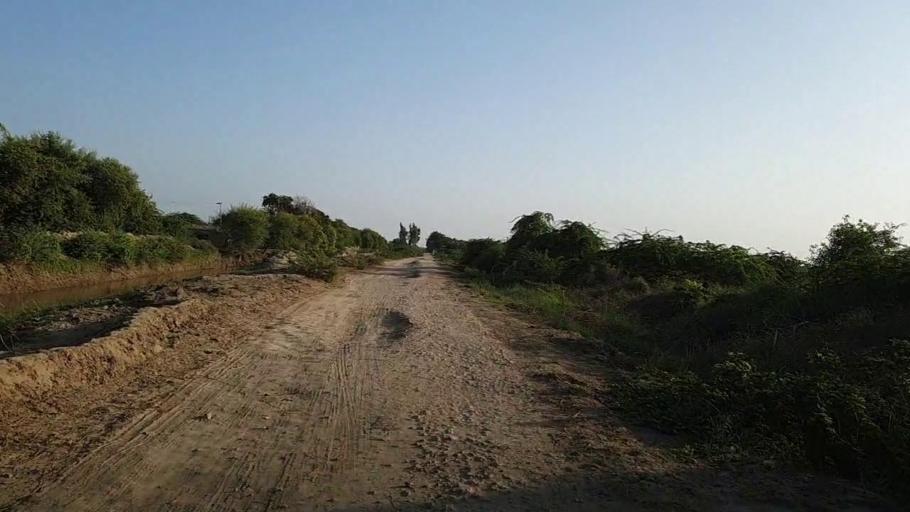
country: PK
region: Sindh
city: Kario
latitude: 24.7246
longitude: 68.6674
